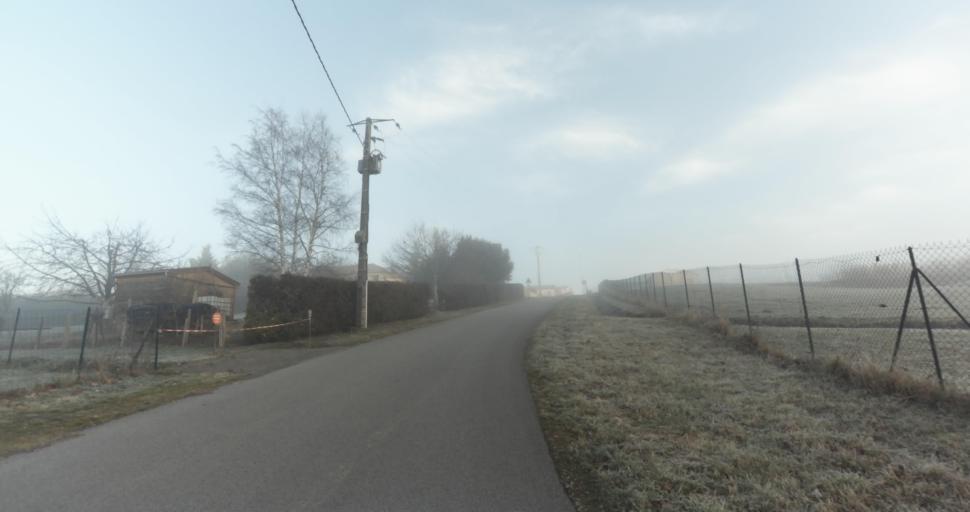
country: FR
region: Limousin
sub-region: Departement de la Haute-Vienne
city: Aixe-sur-Vienne
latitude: 45.7915
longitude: 1.1608
